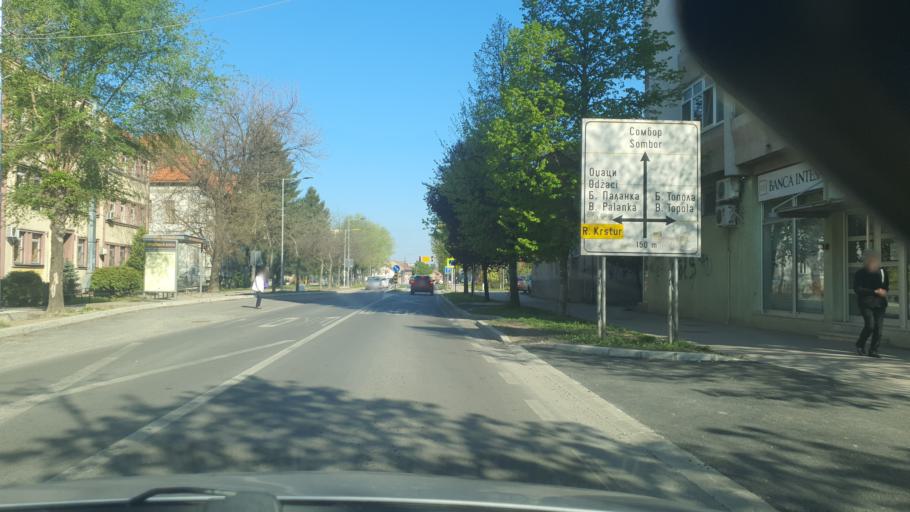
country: RS
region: Autonomna Pokrajina Vojvodina
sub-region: Zapadnobacki Okrug
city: Kula
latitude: 45.6117
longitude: 19.5291
